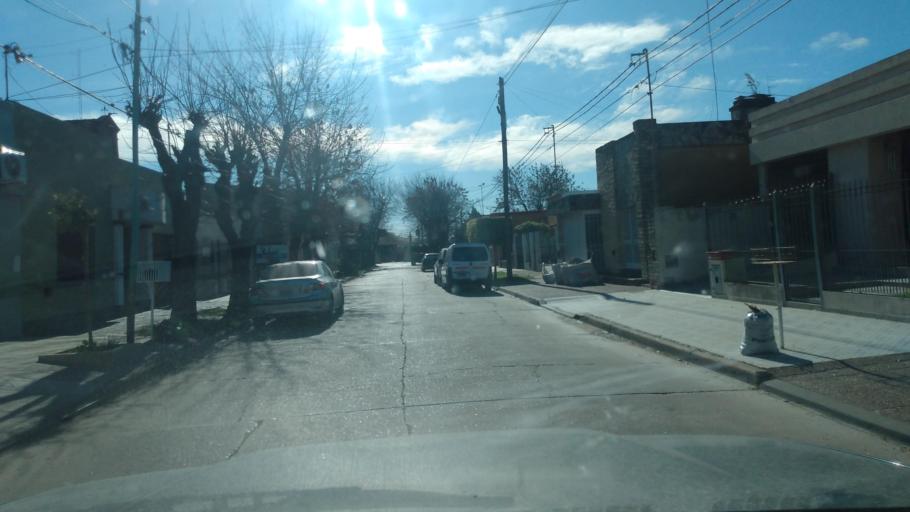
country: AR
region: Buenos Aires
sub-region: Partido de Lujan
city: Lujan
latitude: -34.5653
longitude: -59.1001
